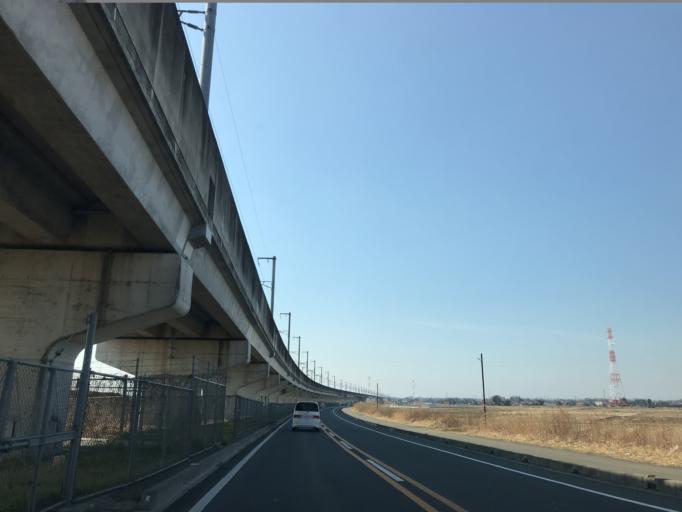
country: JP
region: Ibaraki
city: Mitsukaido
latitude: 35.9866
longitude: 140.0333
